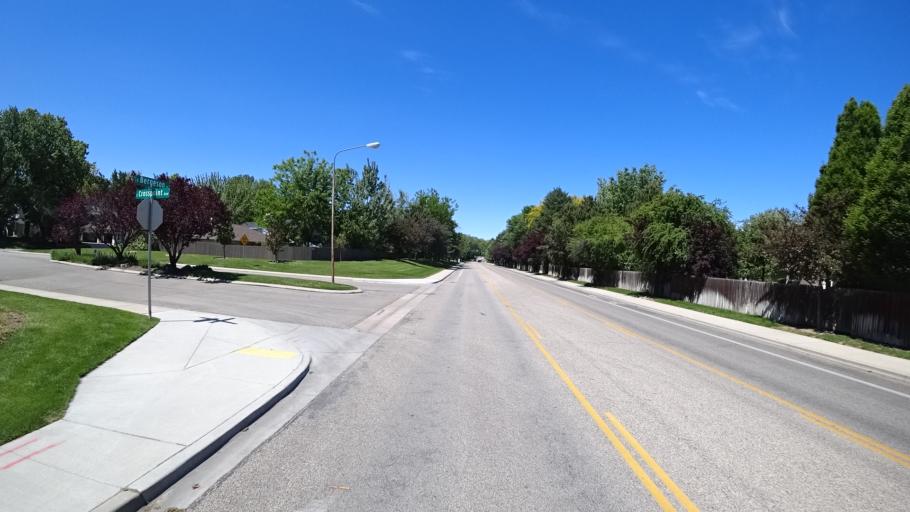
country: US
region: Idaho
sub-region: Ada County
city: Boise
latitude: 43.5678
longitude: -116.1754
